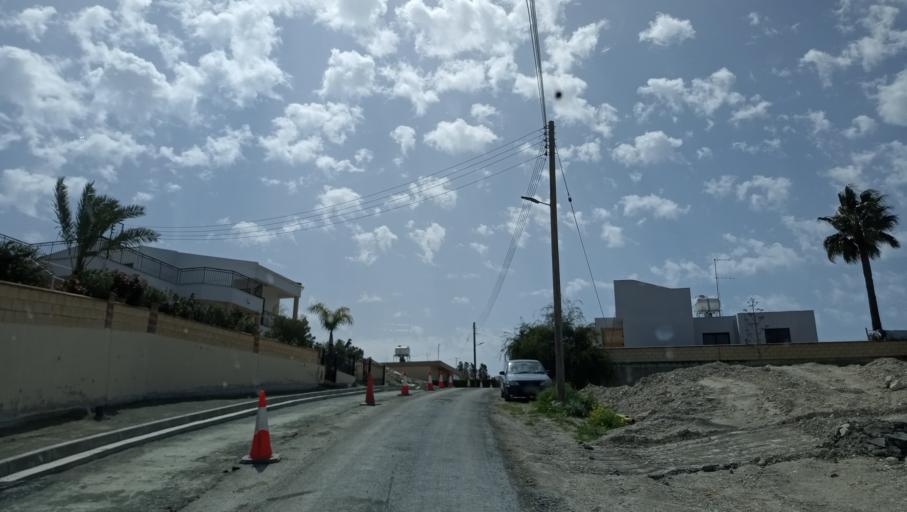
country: CY
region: Lefkosia
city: Dali
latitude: 35.0139
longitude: 33.4210
